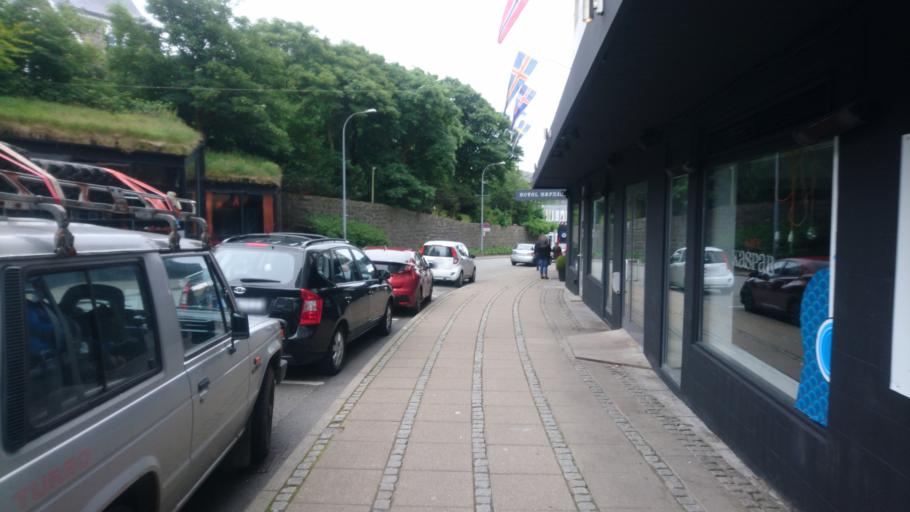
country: FO
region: Streymoy
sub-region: Torshavn
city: Torshavn
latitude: 62.0100
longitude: -6.7710
